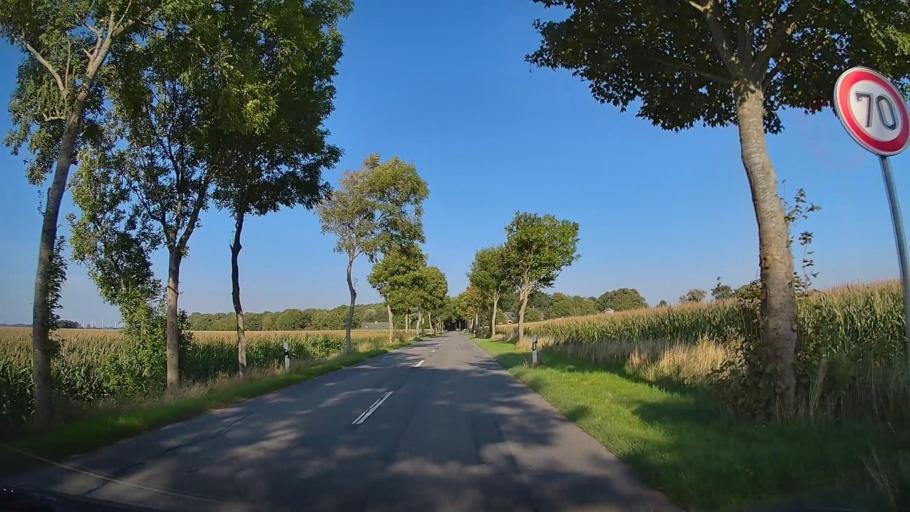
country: DE
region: Lower Saxony
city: Cappel
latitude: 53.7615
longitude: 8.5650
